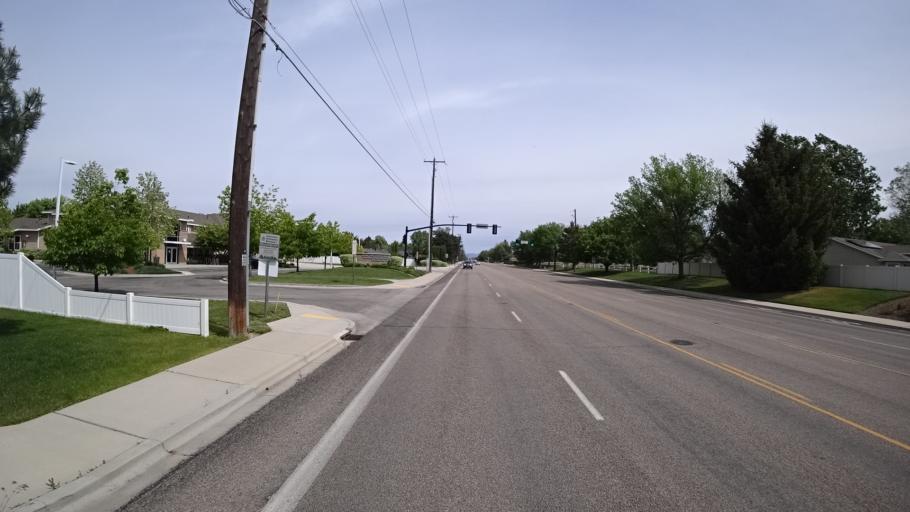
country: US
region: Idaho
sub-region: Ada County
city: Meridian
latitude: 43.5799
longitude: -116.3143
